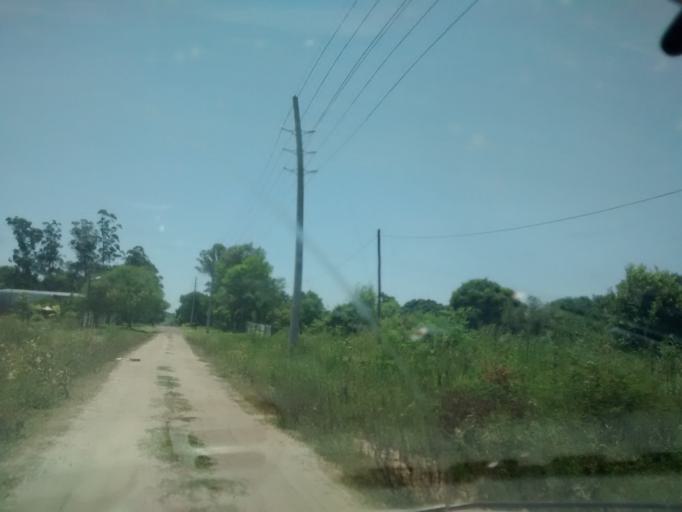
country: AR
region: Chaco
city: Fontana
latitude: -27.4206
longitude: -58.9866
